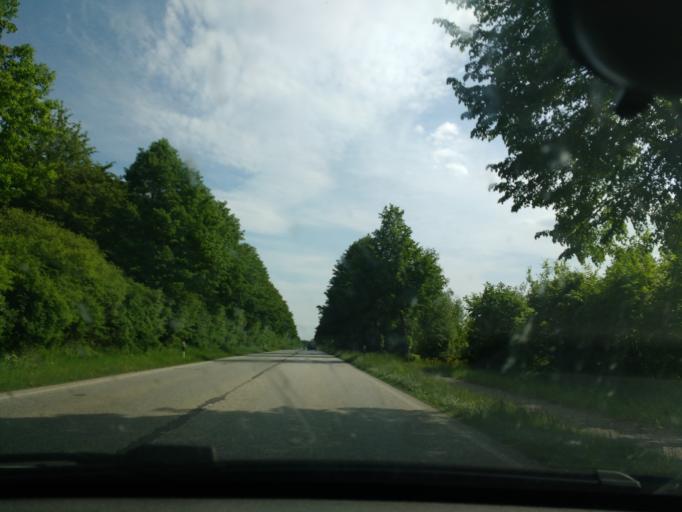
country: DE
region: Schleswig-Holstein
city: Einhaus
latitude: 53.7183
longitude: 10.7340
